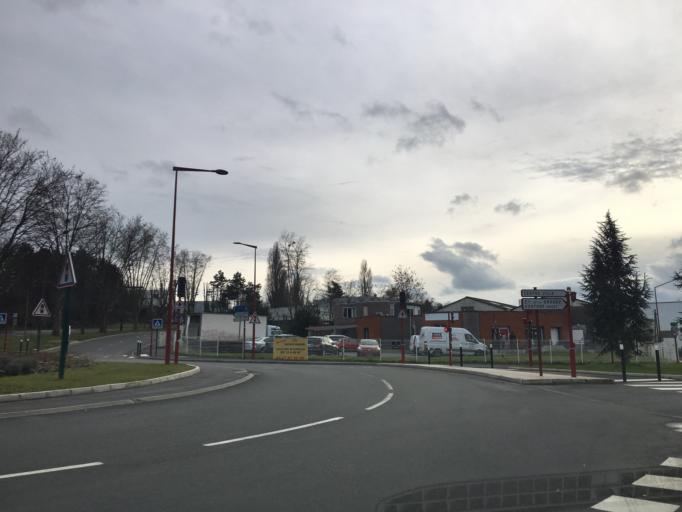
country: FR
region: Ile-de-France
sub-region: Departement du Val-d'Oise
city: Gonesse
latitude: 48.9856
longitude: 2.4595
